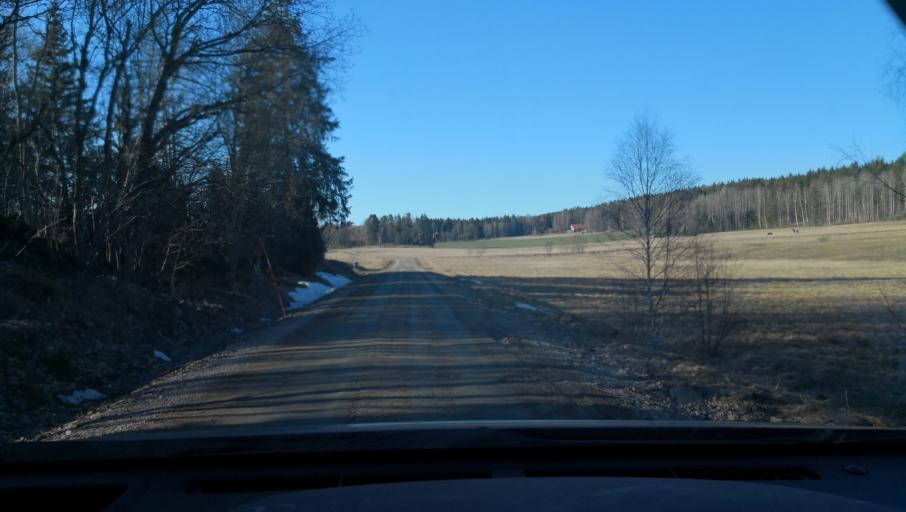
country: SE
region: Vaestmanland
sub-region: Sala Kommun
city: Sala
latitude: 60.1474
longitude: 16.6417
